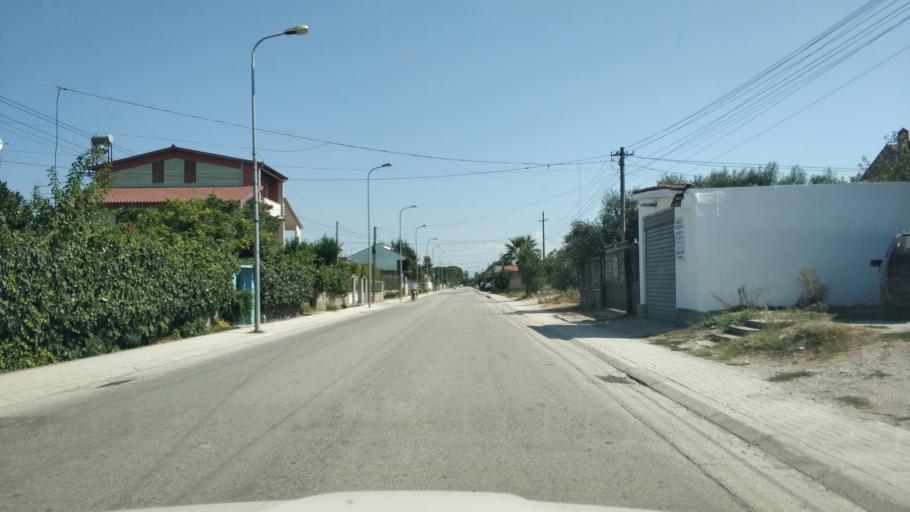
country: AL
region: Fier
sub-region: Rrethi i Lushnjes
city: Gradishte
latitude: 40.8936
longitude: 19.6248
